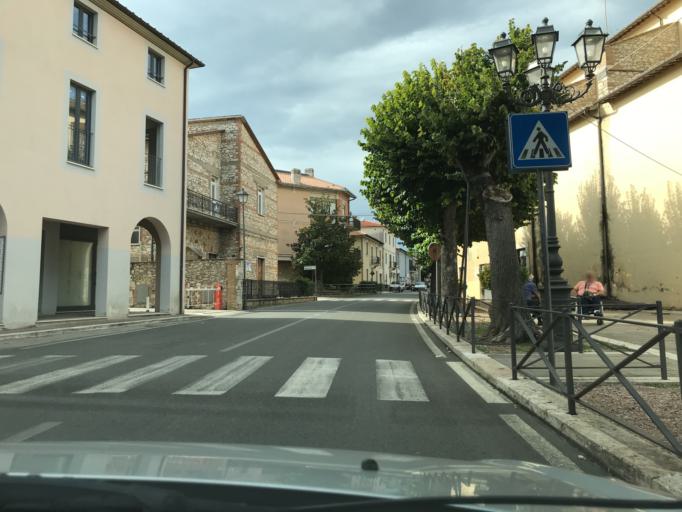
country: IT
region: Umbria
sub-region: Provincia di Terni
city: Guardea
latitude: 42.6235
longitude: 12.2966
